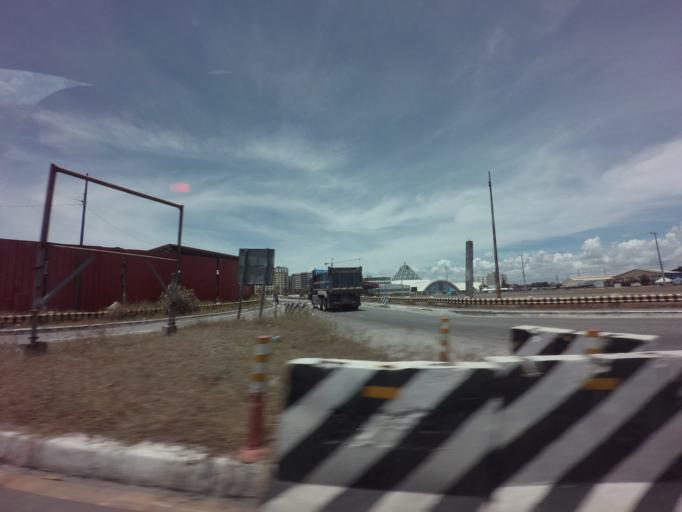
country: PH
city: Sambayanihan People's Village
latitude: 14.4927
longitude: 120.9955
